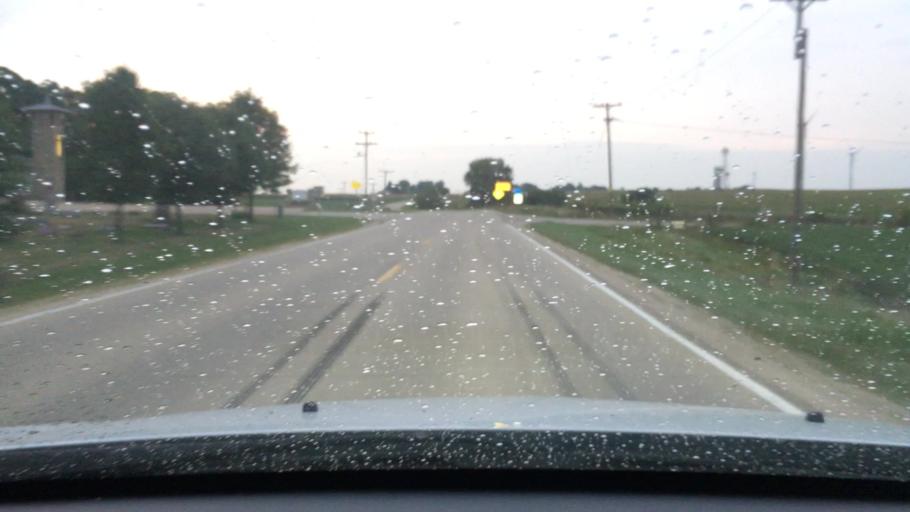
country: US
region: Illinois
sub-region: DeKalb County
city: Malta
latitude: 41.8483
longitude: -88.9420
